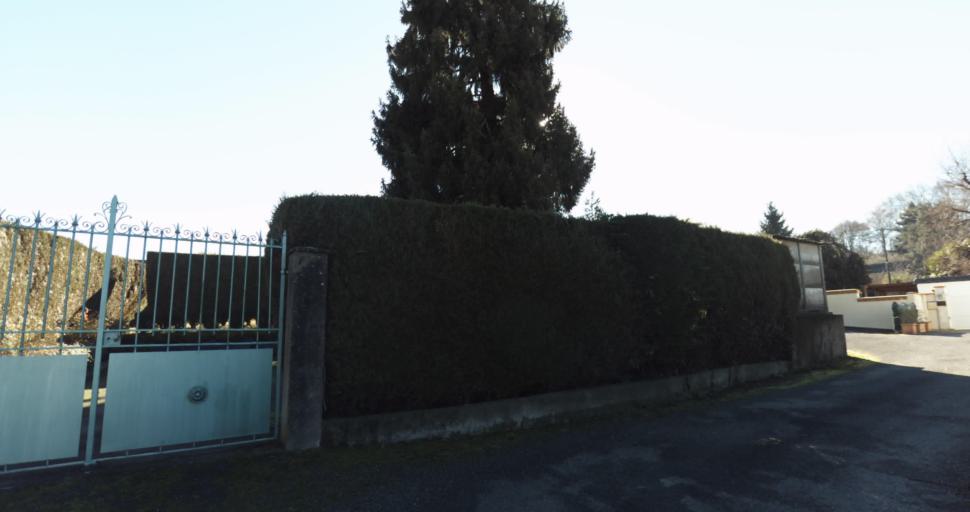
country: FR
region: Aquitaine
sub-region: Departement des Pyrenees-Atlantiques
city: Morlaas
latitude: 43.3431
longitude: -0.2672
